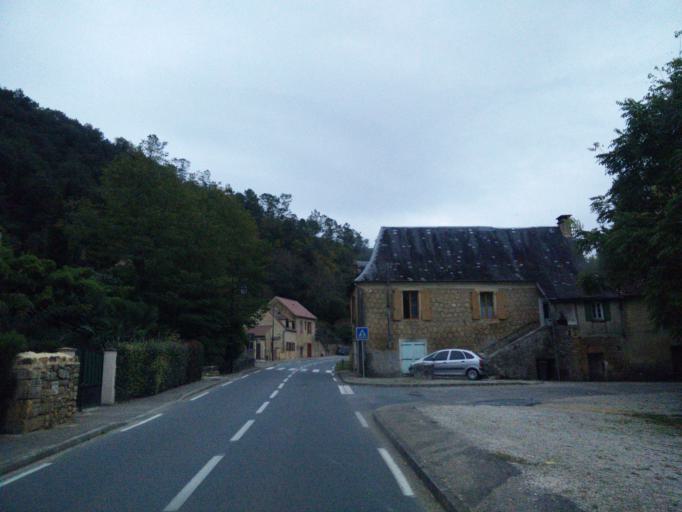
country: FR
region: Aquitaine
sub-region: Departement de la Dordogne
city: Carsac-Aillac
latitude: 44.8096
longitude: 1.2967
